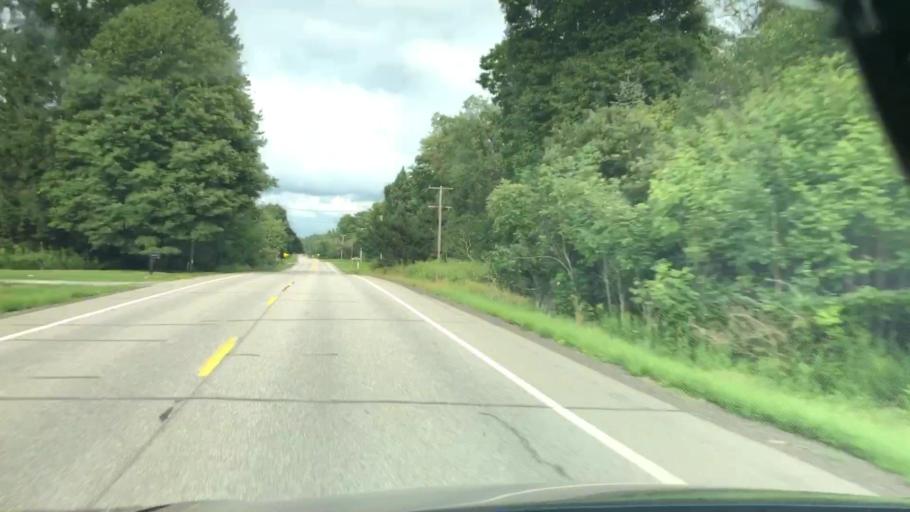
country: US
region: Pennsylvania
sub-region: Erie County
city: Northwest Harborcreek
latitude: 42.0585
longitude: -79.8891
